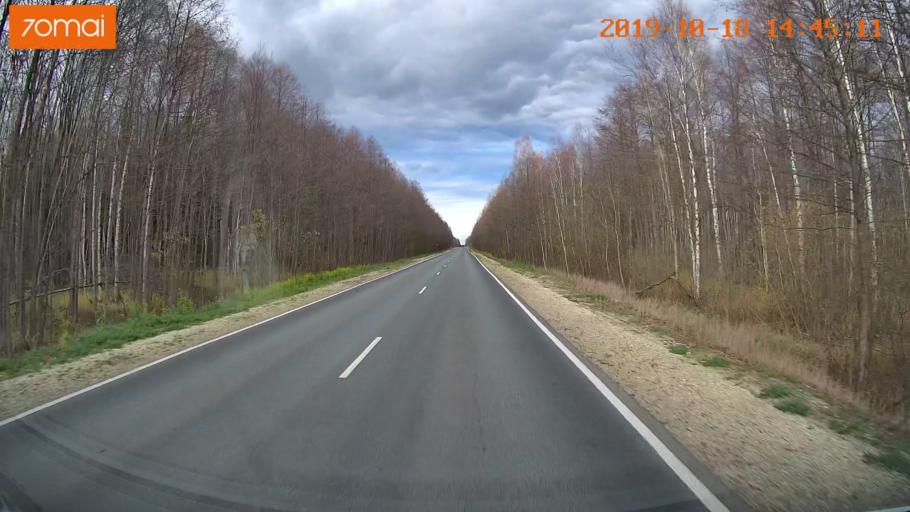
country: RU
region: Vladimir
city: Velikodvorskiy
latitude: 55.3507
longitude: 40.6784
